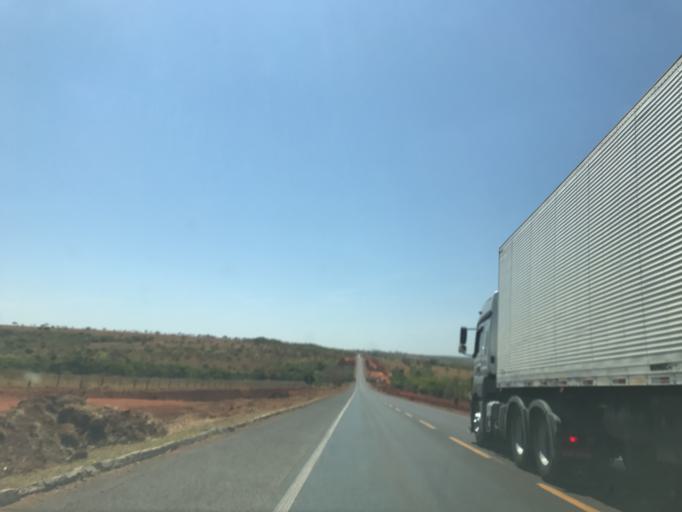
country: BR
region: Minas Gerais
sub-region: Prata
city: Prata
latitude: -19.4418
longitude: -48.8888
